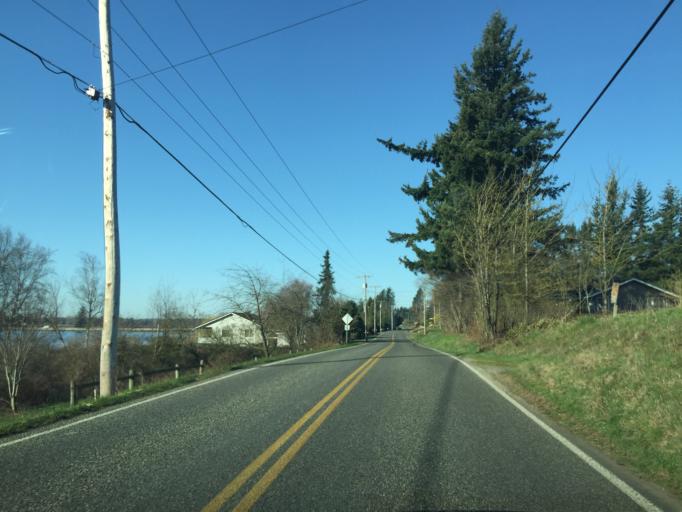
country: US
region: Washington
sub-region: Whatcom County
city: Lynden
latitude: 48.9065
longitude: -122.4766
